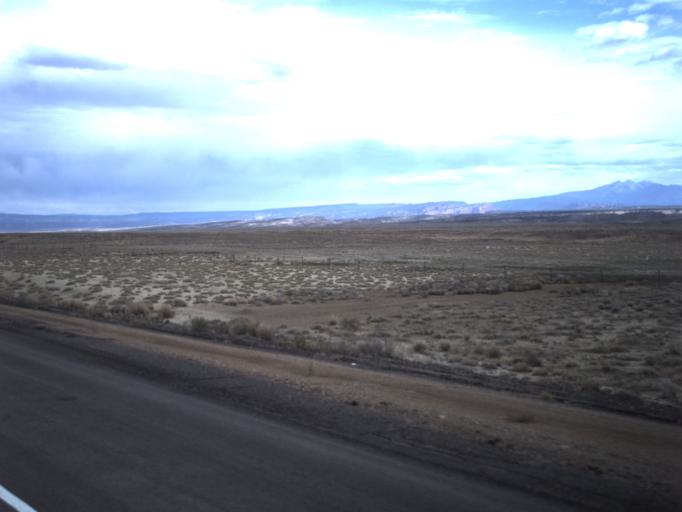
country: US
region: Utah
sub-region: Grand County
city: Moab
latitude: 38.9378
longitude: -109.4924
